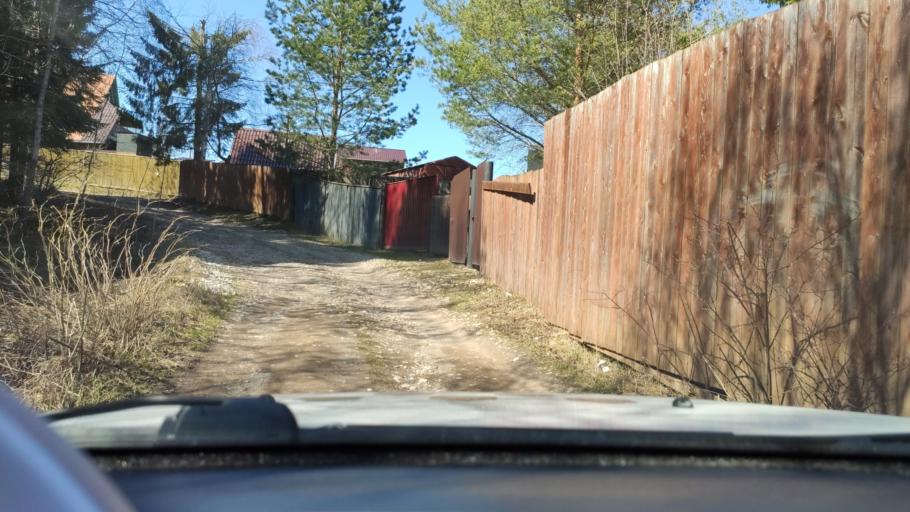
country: RU
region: Perm
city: Novyye Lyady
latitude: 58.0492
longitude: 56.6508
